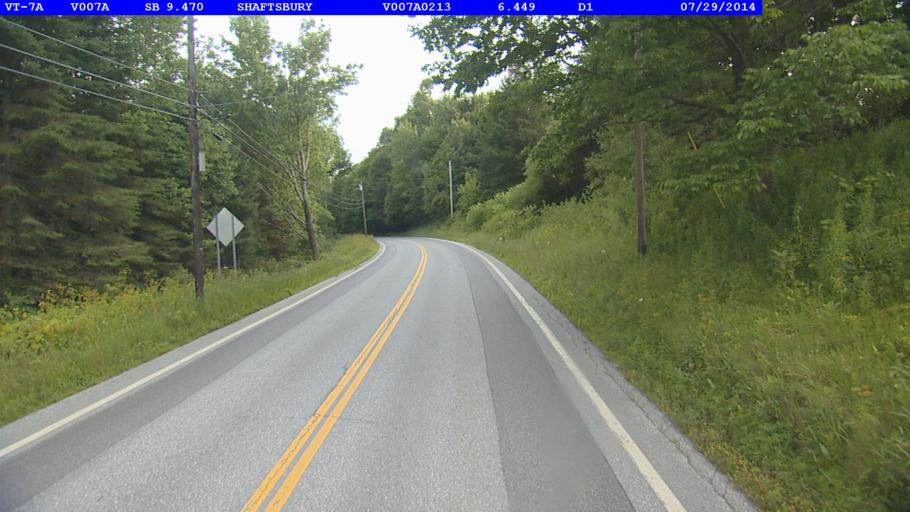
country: US
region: Vermont
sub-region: Bennington County
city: Arlington
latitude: 43.0217
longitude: -73.1899
